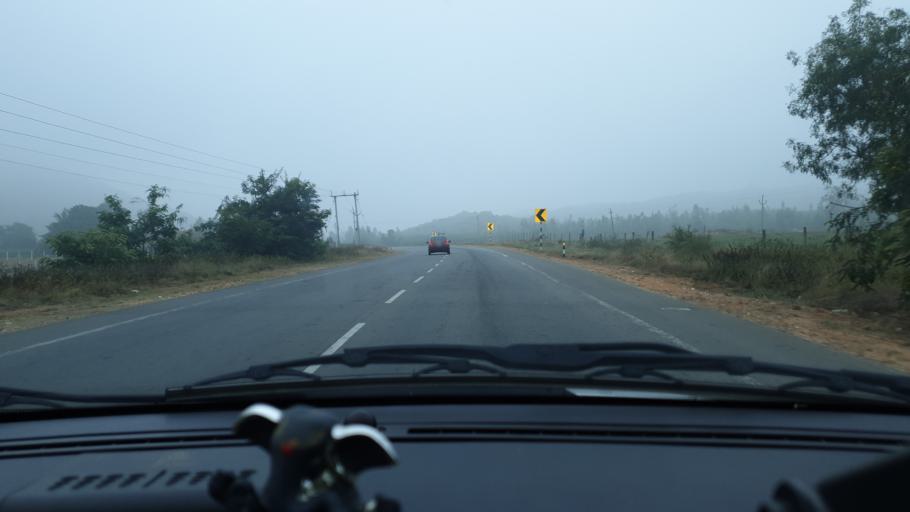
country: IN
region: Telangana
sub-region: Mahbubnagar
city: Farrukhnagar
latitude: 16.9141
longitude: 78.5270
